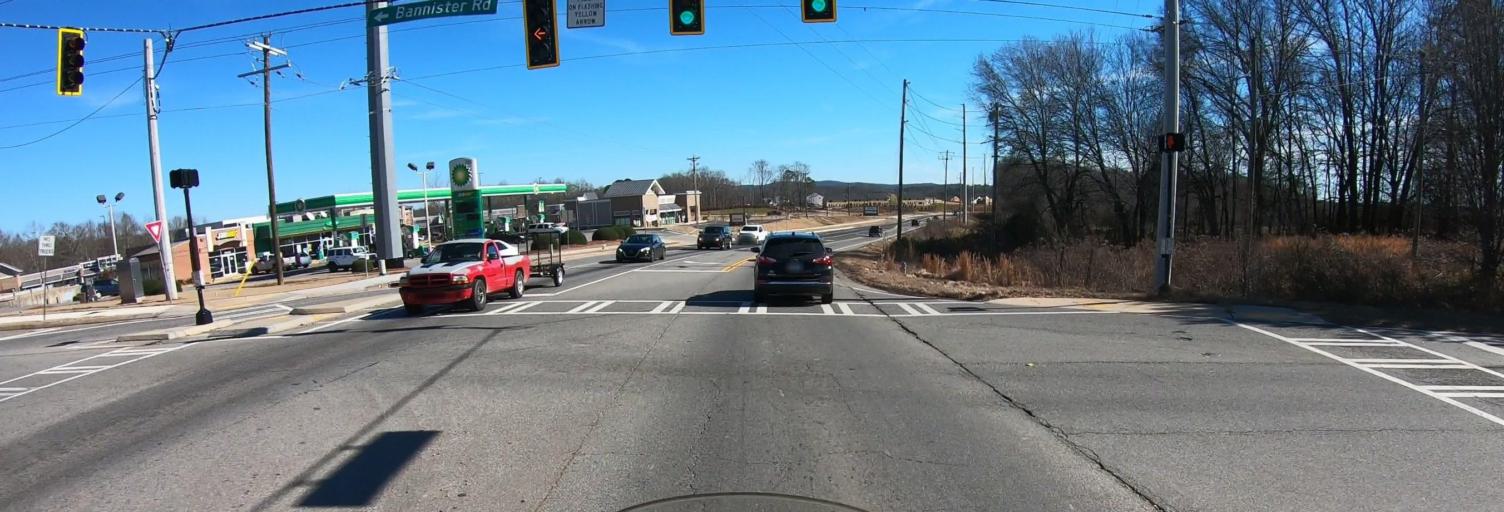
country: US
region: Georgia
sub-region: Forsyth County
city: Cumming
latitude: 34.2942
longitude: -84.1565
